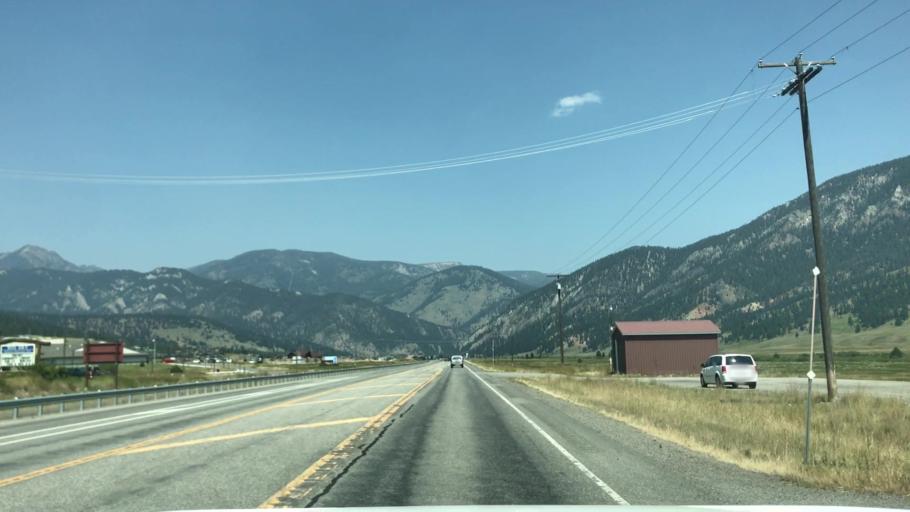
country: US
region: Montana
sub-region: Gallatin County
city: Big Sky
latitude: 45.2284
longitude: -111.2508
